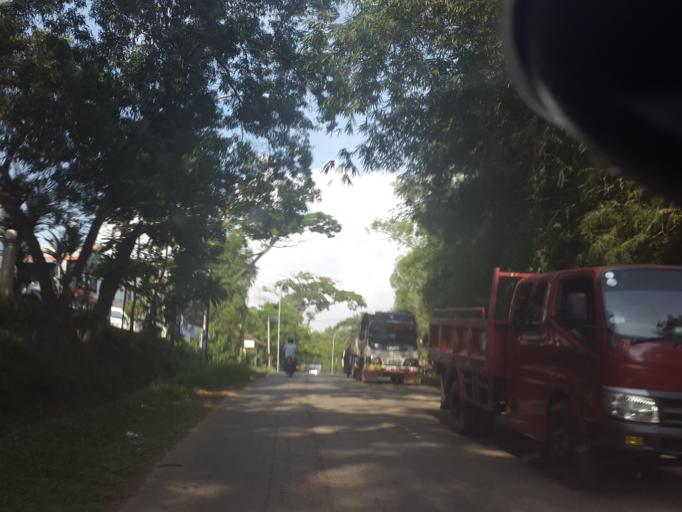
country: SG
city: Singapore
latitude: 1.1606
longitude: 104.0170
